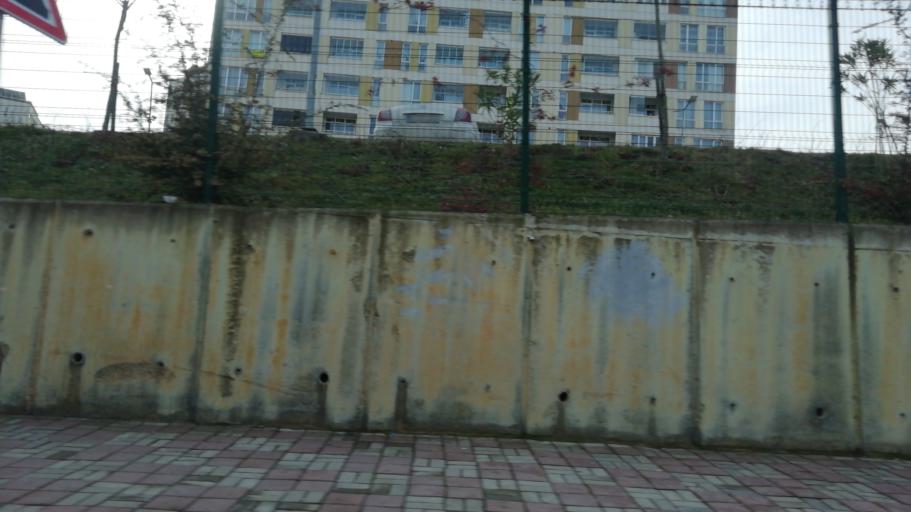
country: TR
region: Istanbul
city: Basaksehir
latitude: 41.1286
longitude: 28.7795
